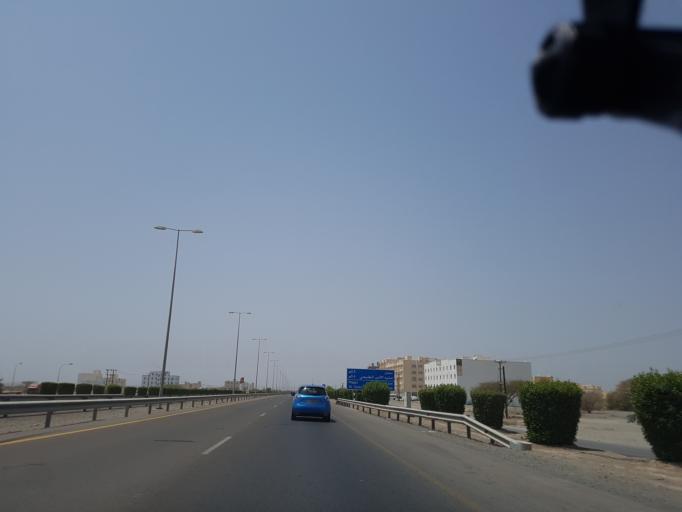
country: OM
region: Al Batinah
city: Al Liwa'
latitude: 24.4180
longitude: 56.6045
